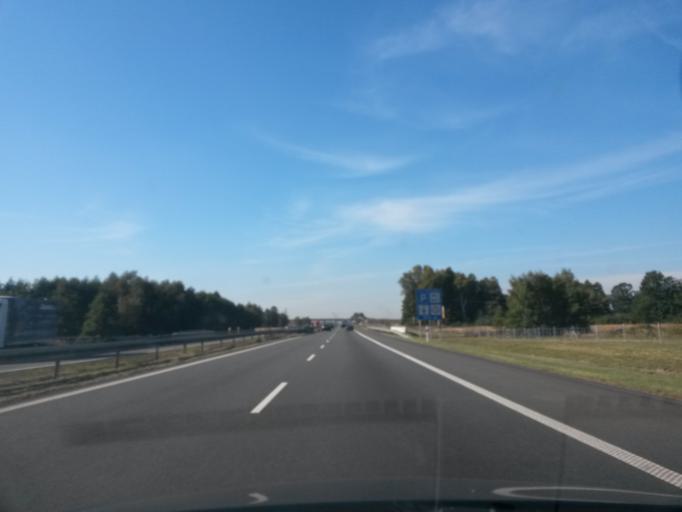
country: PL
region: Opole Voivodeship
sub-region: Powiat opolski
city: Proszkow
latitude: 50.5630
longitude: 17.8715
